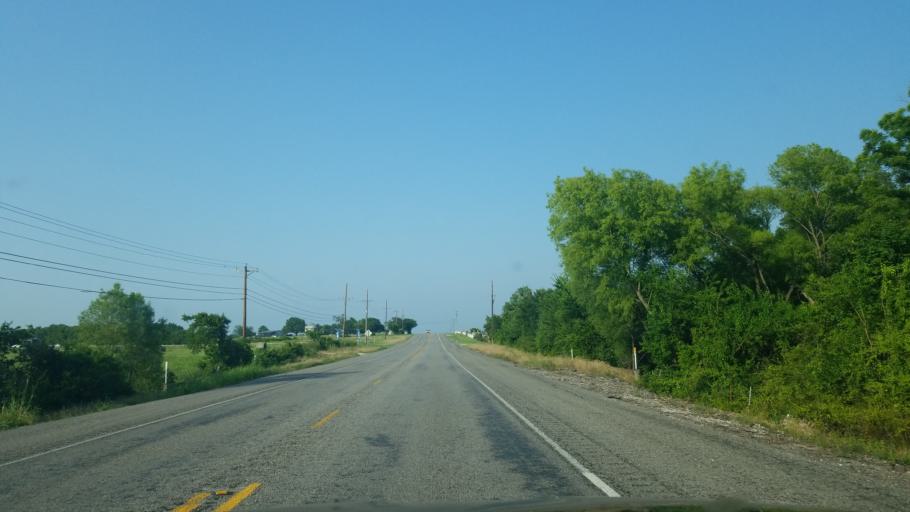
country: US
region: Texas
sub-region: Denton County
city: Krugerville
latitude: 33.2968
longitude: -97.0744
